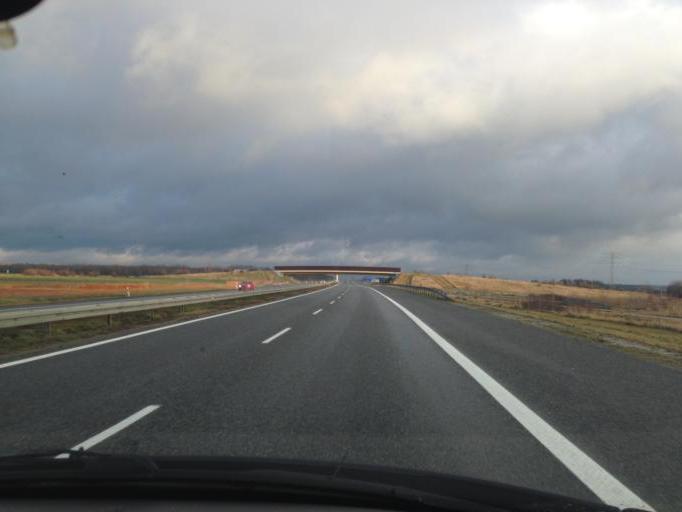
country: PL
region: Silesian Voivodeship
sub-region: Powiat gliwicki
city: Zernica
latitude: 50.2659
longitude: 18.5939
